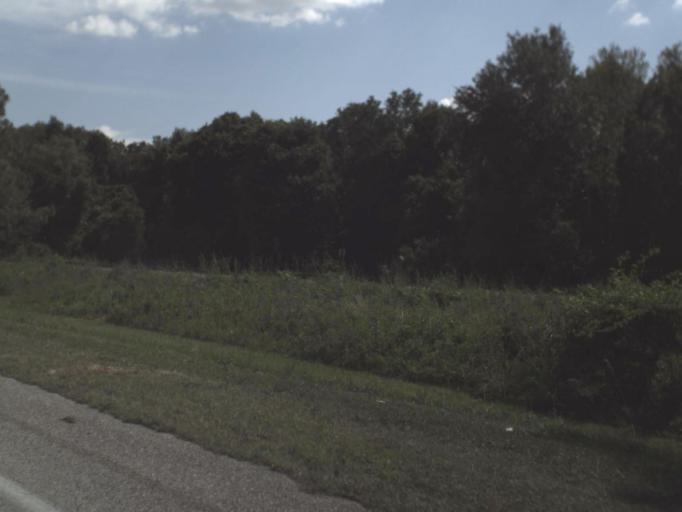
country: US
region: Florida
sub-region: Alachua County
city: Hawthorne
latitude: 29.5229
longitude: -82.1028
